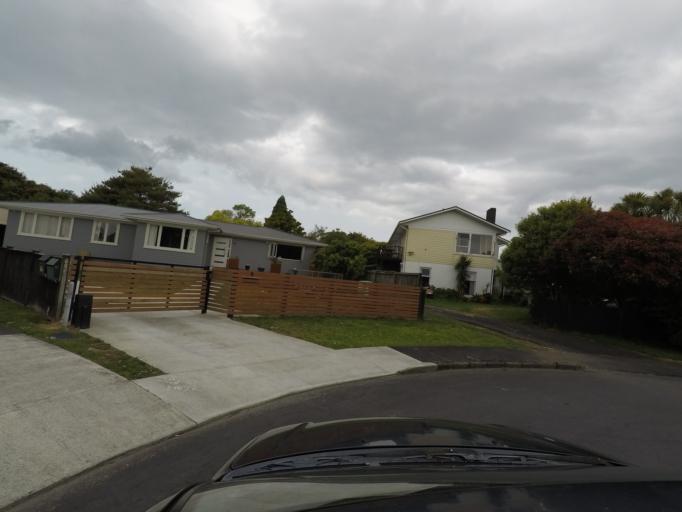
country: NZ
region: Auckland
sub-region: Auckland
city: Rosebank
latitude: -36.8468
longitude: 174.6489
